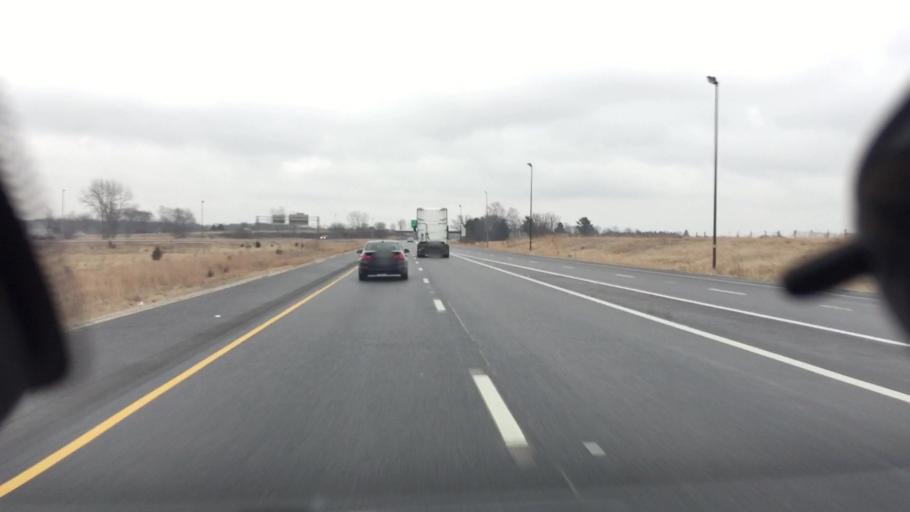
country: US
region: Illinois
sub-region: Tazewell County
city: Morton
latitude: 40.6306
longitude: -89.5152
